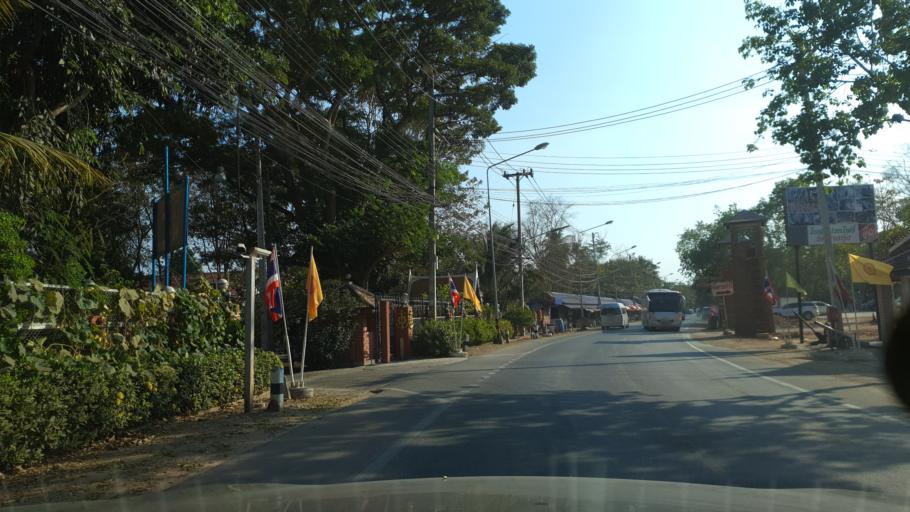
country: TH
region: Samut Songkhram
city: Bang Khon Thi
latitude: 13.4464
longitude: 99.9418
